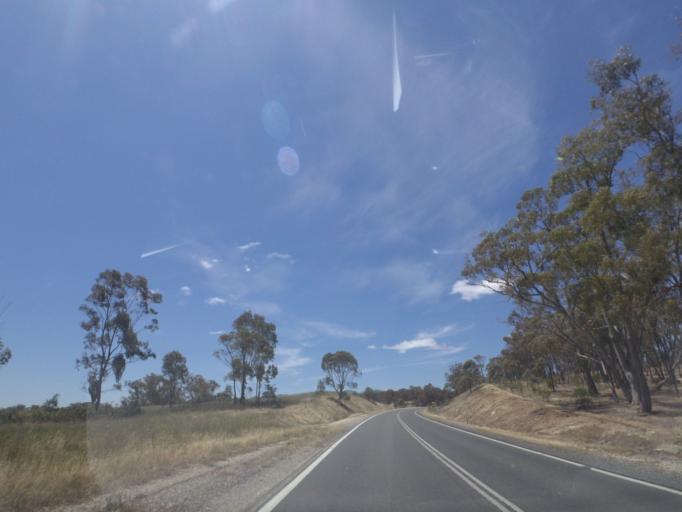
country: AU
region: Victoria
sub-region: Mount Alexander
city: Castlemaine
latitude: -37.1670
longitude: 144.1478
